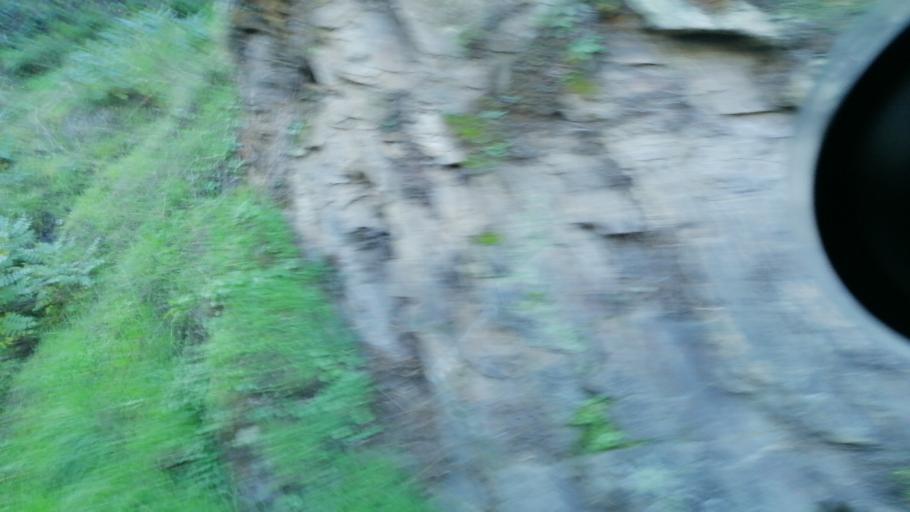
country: PT
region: Vila Real
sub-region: Peso da Regua
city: Peso da Regua
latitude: 41.1419
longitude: -7.7793
